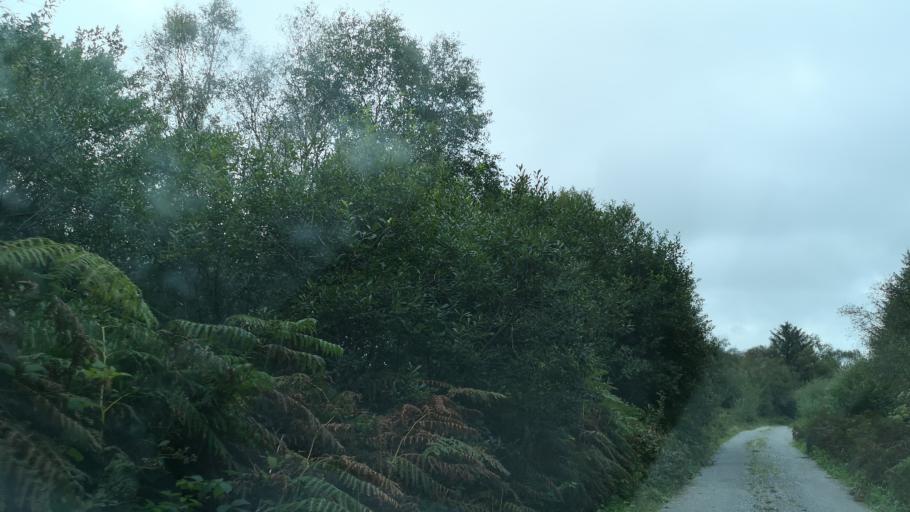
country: IE
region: Connaught
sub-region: County Galway
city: Athenry
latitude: 53.3019
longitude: -8.6671
